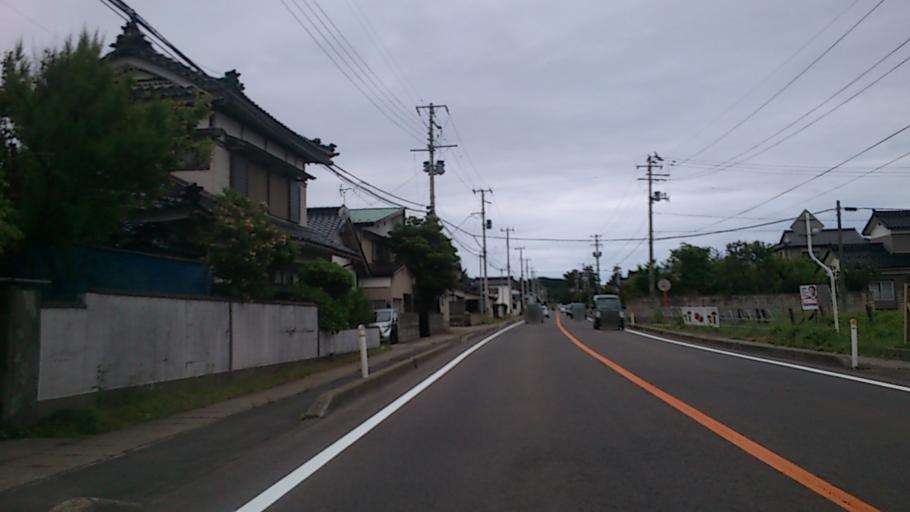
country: JP
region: Yamagata
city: Yuza
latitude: 39.3446
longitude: 140.0109
